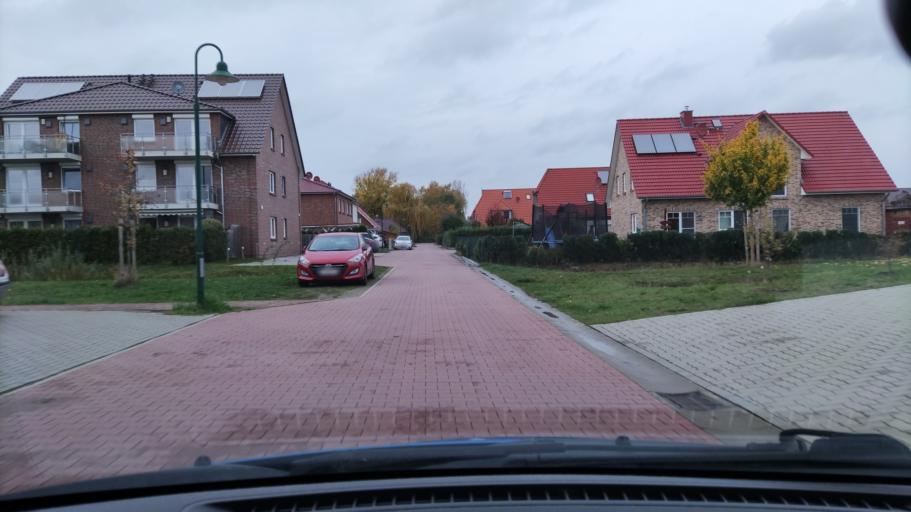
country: DE
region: Schleswig-Holstein
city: Escheburg
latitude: 53.4246
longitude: 10.3166
